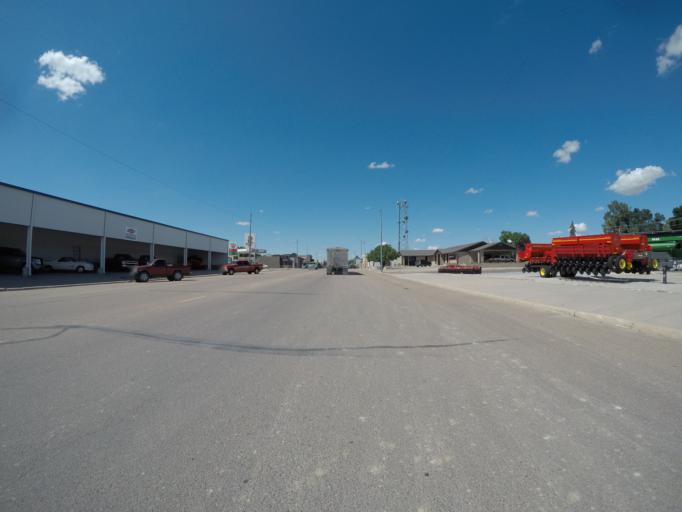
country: US
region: Nebraska
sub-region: Chase County
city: Imperial
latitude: 40.5140
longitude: -101.6431
